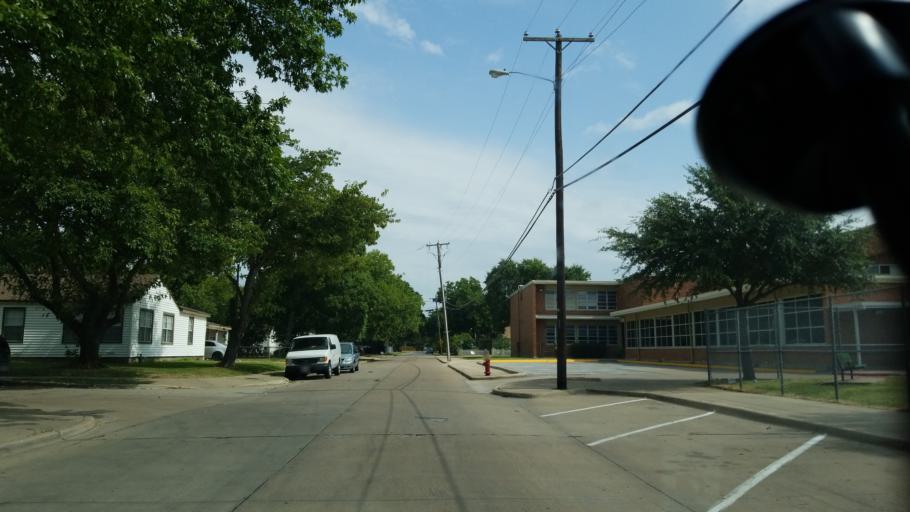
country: US
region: Texas
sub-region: Dallas County
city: Grand Prairie
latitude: 32.7514
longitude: -96.9886
